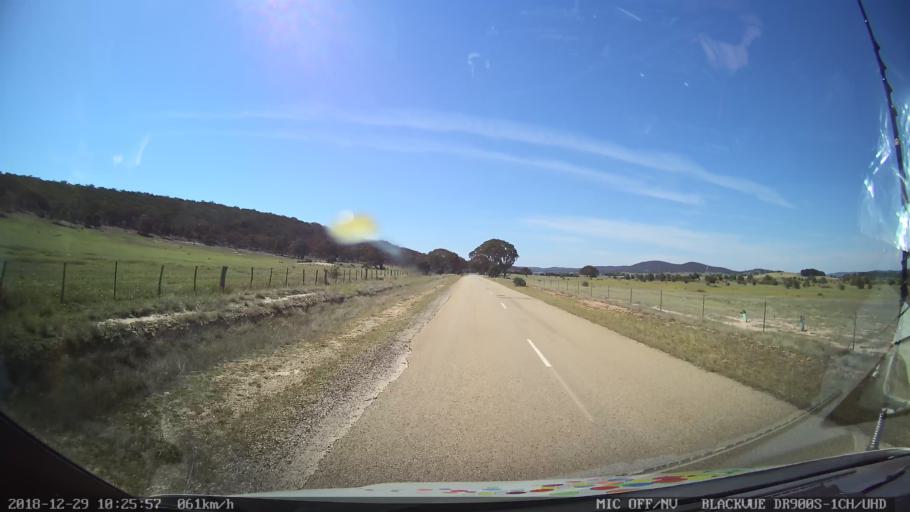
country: AU
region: New South Wales
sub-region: Yass Valley
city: Gundaroo
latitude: -34.9213
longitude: 149.4407
